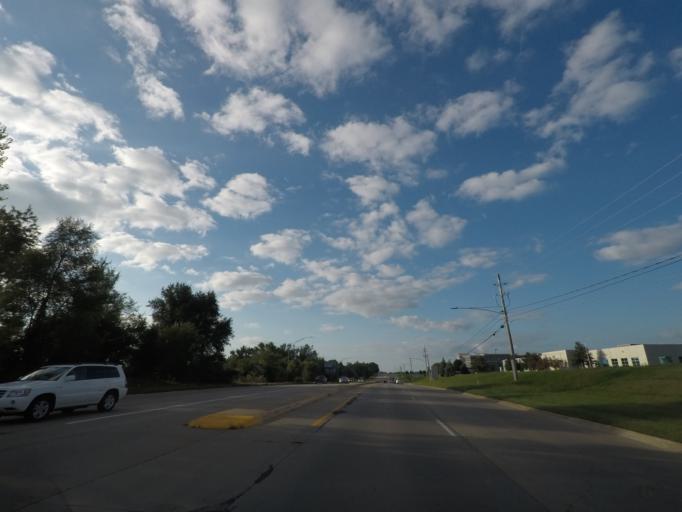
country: US
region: Iowa
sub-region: Warren County
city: Norwalk
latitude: 41.5213
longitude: -93.6450
